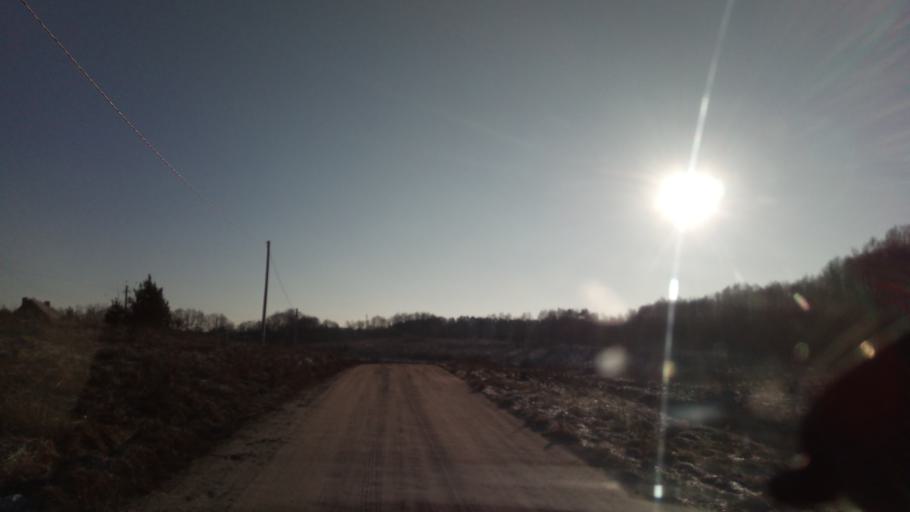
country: LT
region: Alytaus apskritis
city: Druskininkai
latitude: 54.1051
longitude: 24.0121
